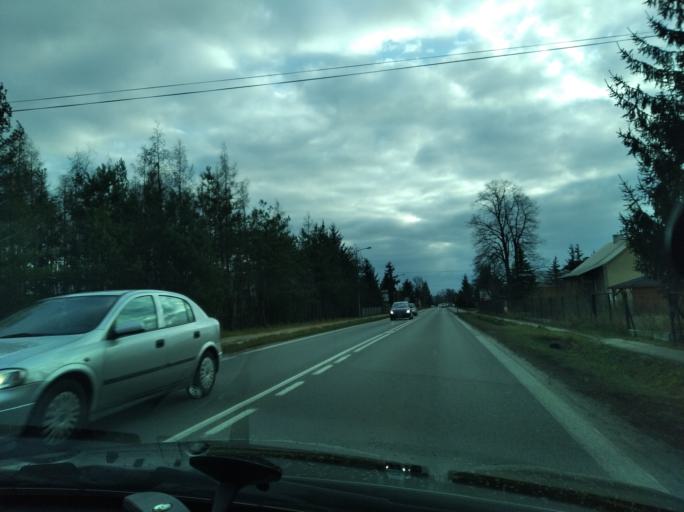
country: PL
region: Subcarpathian Voivodeship
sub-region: Powiat lancucki
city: Rakszawa
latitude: 50.1203
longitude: 22.2323
